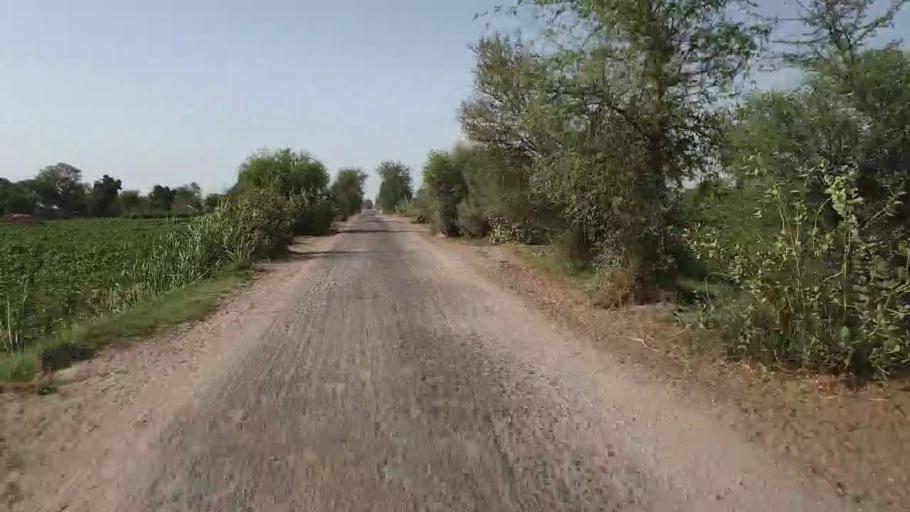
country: PK
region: Sindh
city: Kandiari
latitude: 26.6895
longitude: 68.9645
